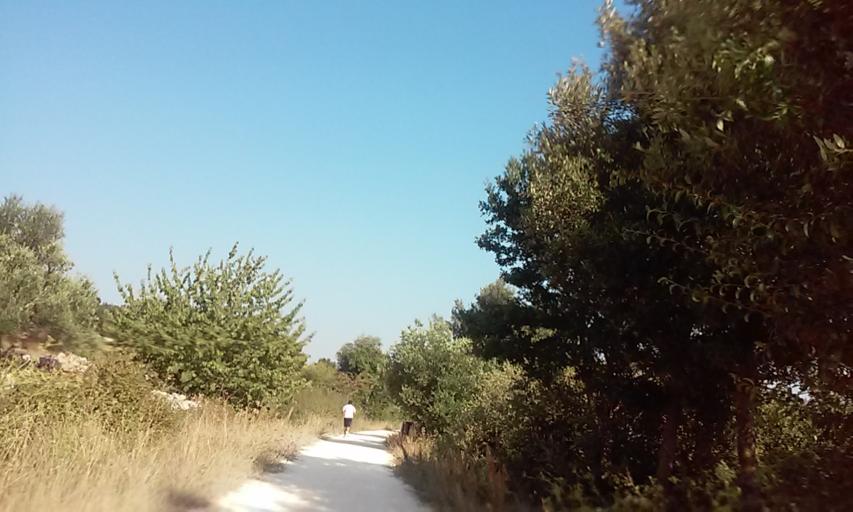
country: IT
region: Apulia
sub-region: Provincia di Brindisi
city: Cisternino
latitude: 40.7053
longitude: 17.4168
